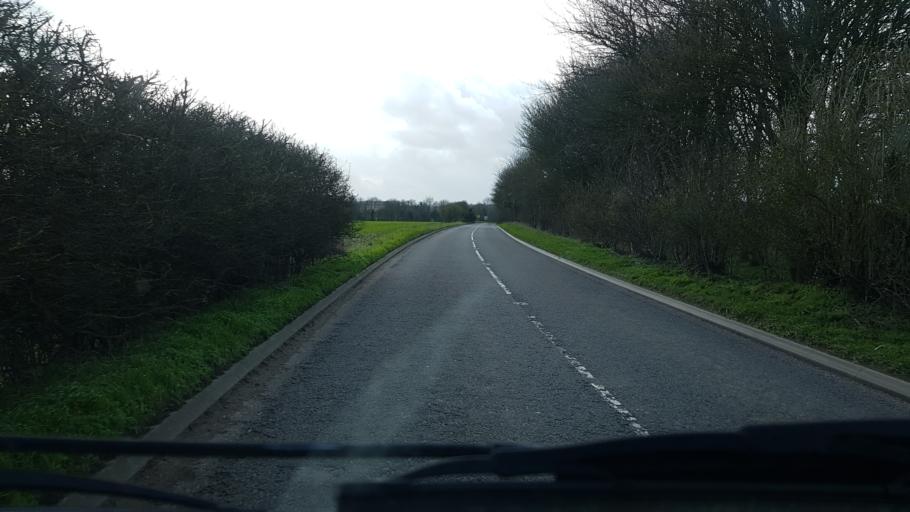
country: GB
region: England
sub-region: Wiltshire
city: Avebury
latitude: 51.4593
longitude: -1.8503
